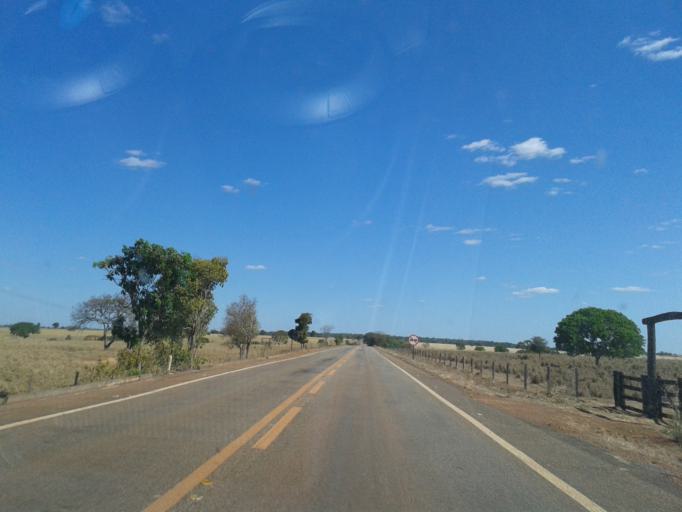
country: BR
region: Goias
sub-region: Sao Miguel Do Araguaia
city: Sao Miguel do Araguaia
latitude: -13.4430
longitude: -50.2904
